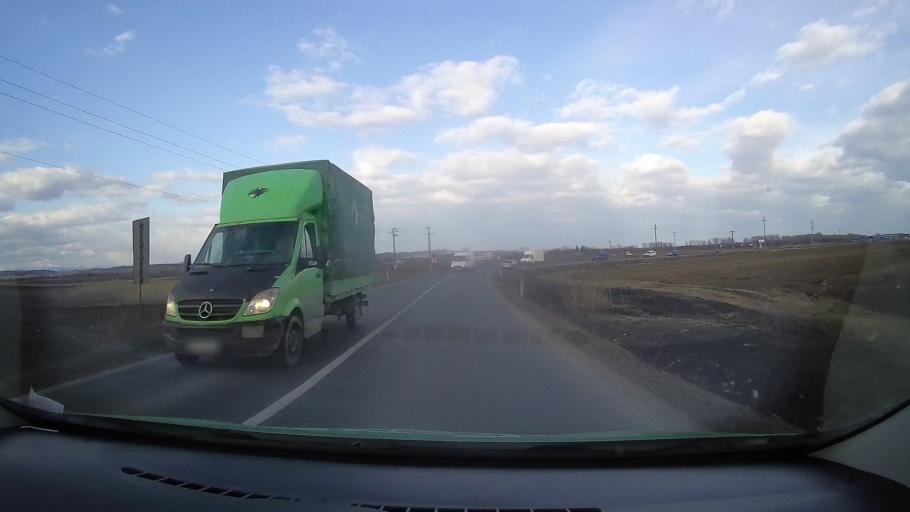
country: RO
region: Dambovita
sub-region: Comuna Ulmi
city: Ulmi
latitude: 44.9041
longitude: 25.5283
